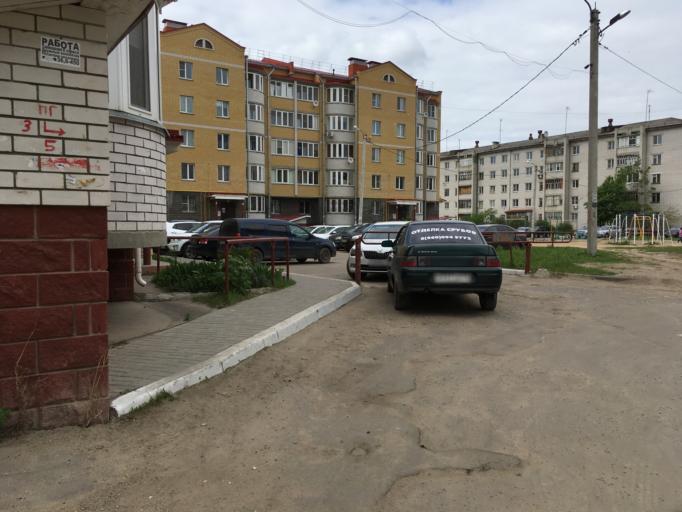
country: RU
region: Mariy-El
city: Yoshkar-Ola
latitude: 56.6480
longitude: 47.8599
